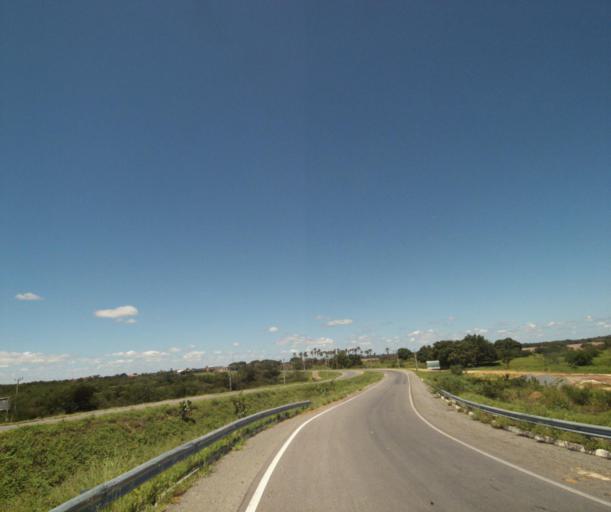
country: BR
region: Bahia
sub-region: Carinhanha
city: Carinhanha
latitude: -14.3288
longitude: -43.7657
